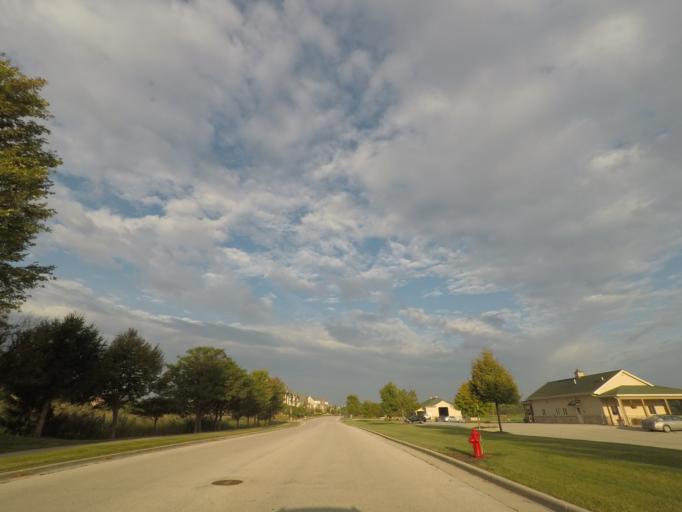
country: US
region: Wisconsin
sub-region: Waukesha County
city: Brookfield
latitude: 43.0393
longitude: -88.1127
